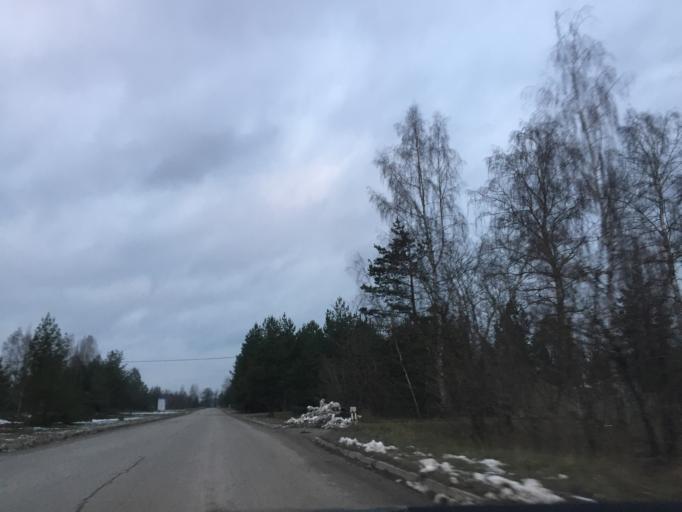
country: LV
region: Stopini
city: Ulbroka
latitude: 56.9006
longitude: 24.2470
